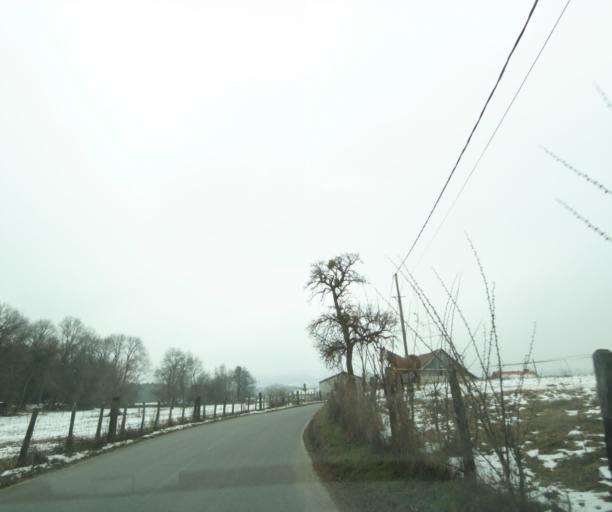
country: FR
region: Rhone-Alpes
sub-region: Departement de la Haute-Savoie
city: Reignier-Esery
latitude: 46.1283
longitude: 6.2850
